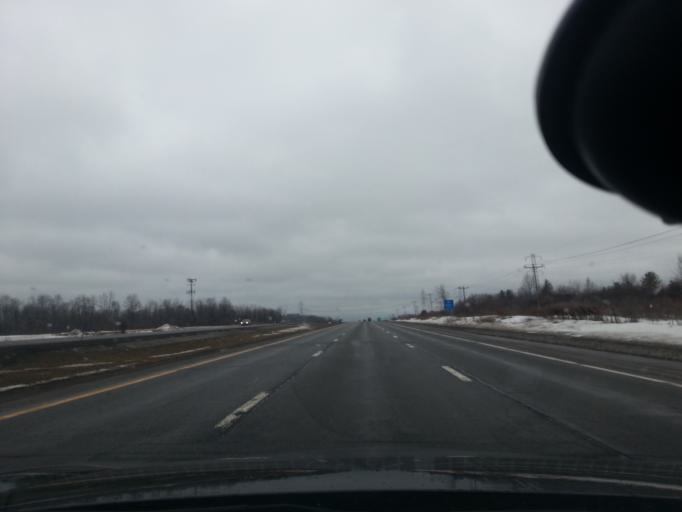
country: US
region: New York
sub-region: Onondaga County
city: Brewerton
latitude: 43.1982
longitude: -76.1246
